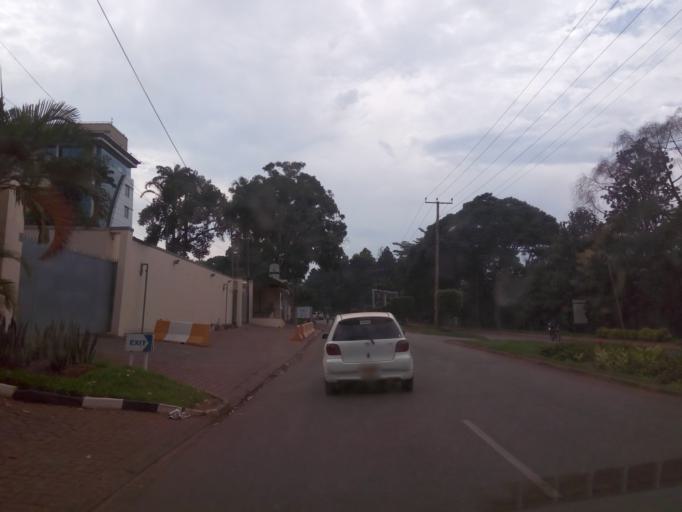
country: UG
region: Central Region
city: Kampala Central Division
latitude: 0.3290
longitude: 32.5827
